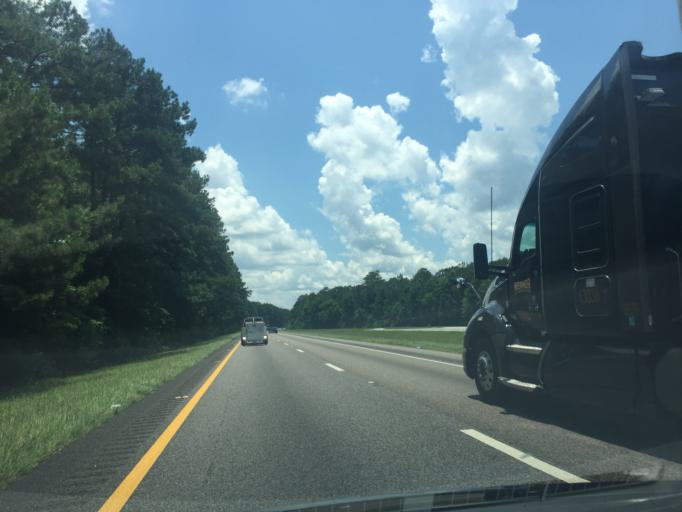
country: US
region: South Carolina
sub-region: Jasper County
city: Hardeeville
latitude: 32.2602
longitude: -81.0961
